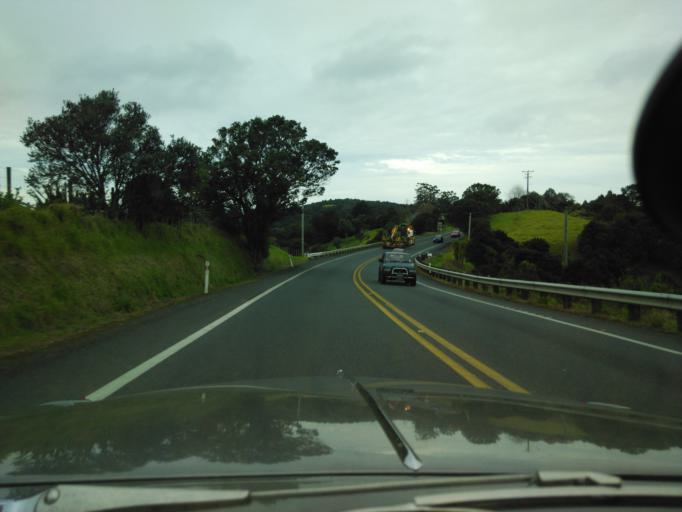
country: NZ
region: Auckland
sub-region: Auckland
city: Warkworth
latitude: -36.5339
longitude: 174.6934
